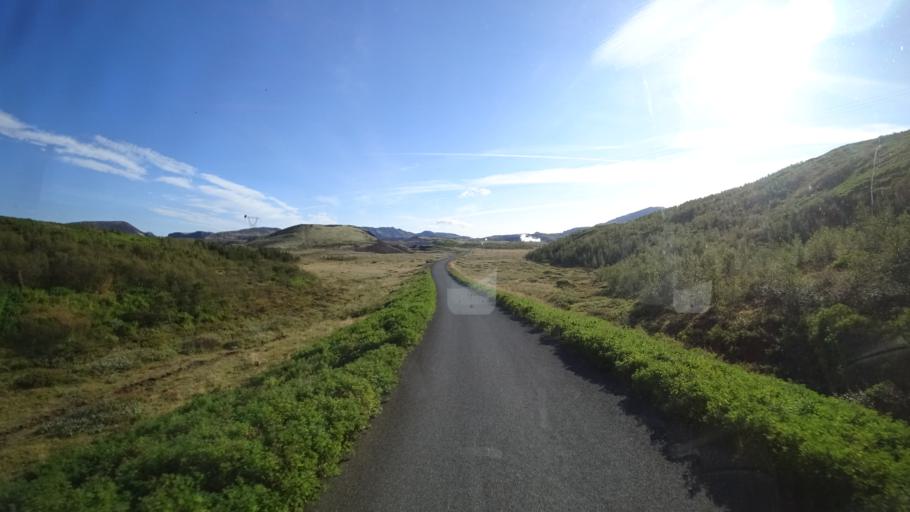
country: IS
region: South
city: Hveragerdi
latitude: 64.1301
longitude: -21.2511
